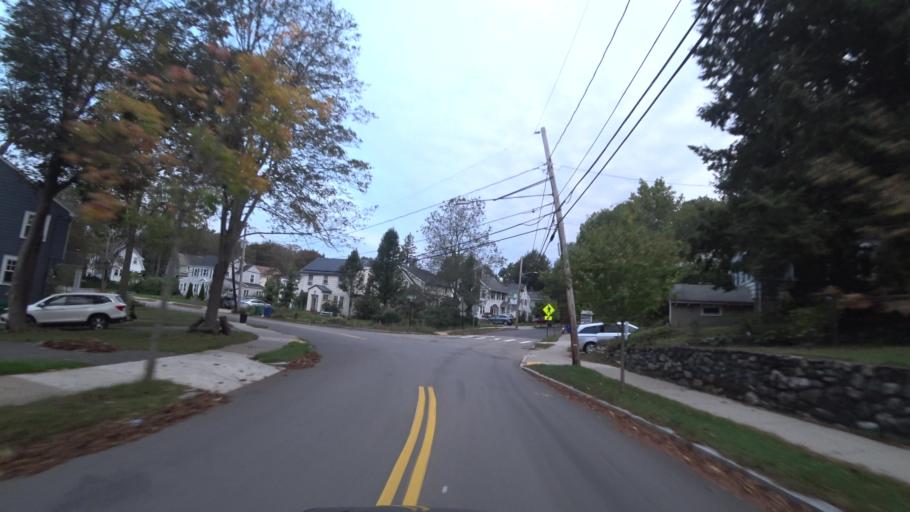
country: US
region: Massachusetts
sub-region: Middlesex County
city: Newton
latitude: 42.3211
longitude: -71.1912
